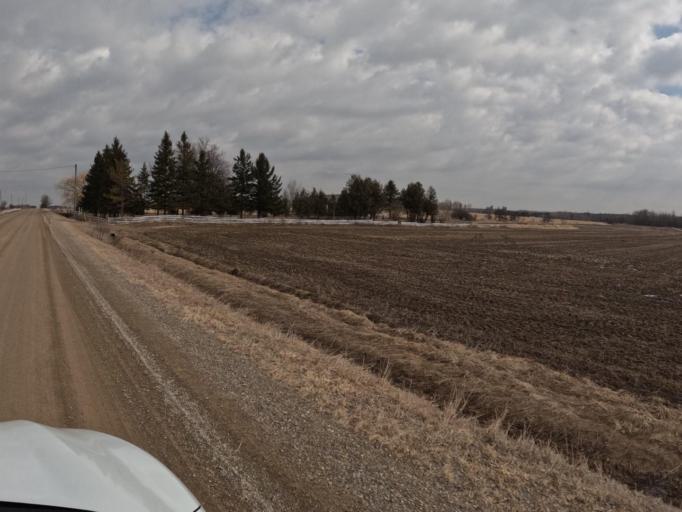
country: CA
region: Ontario
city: Orangeville
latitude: 43.9249
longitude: -80.1865
